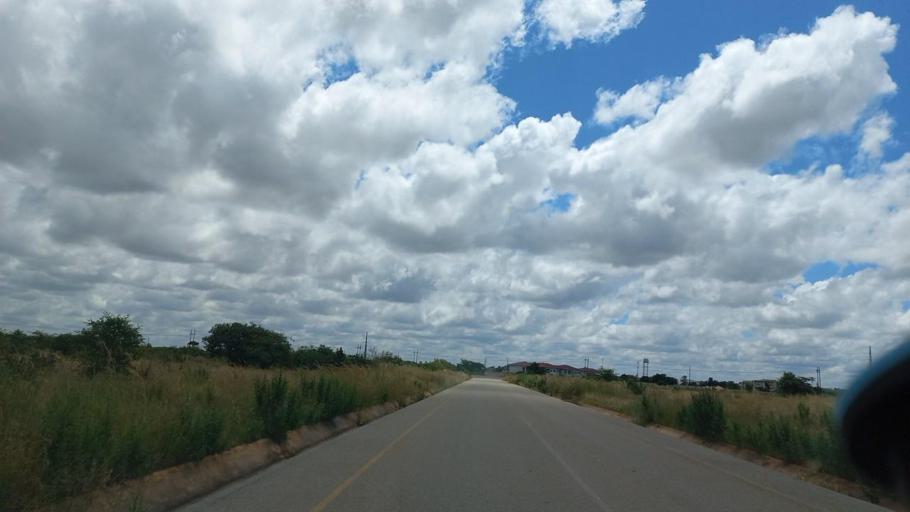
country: ZM
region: Lusaka
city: Lusaka
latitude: -15.4928
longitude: 28.3733
